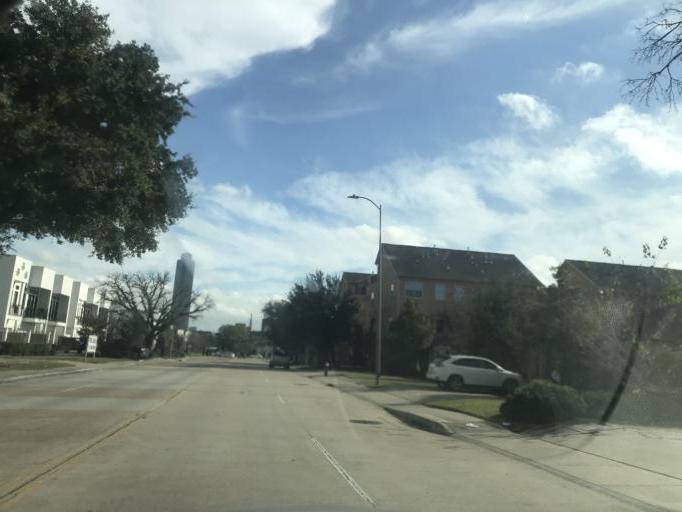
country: US
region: Texas
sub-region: Harris County
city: Bellaire
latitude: 29.7354
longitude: -95.4786
